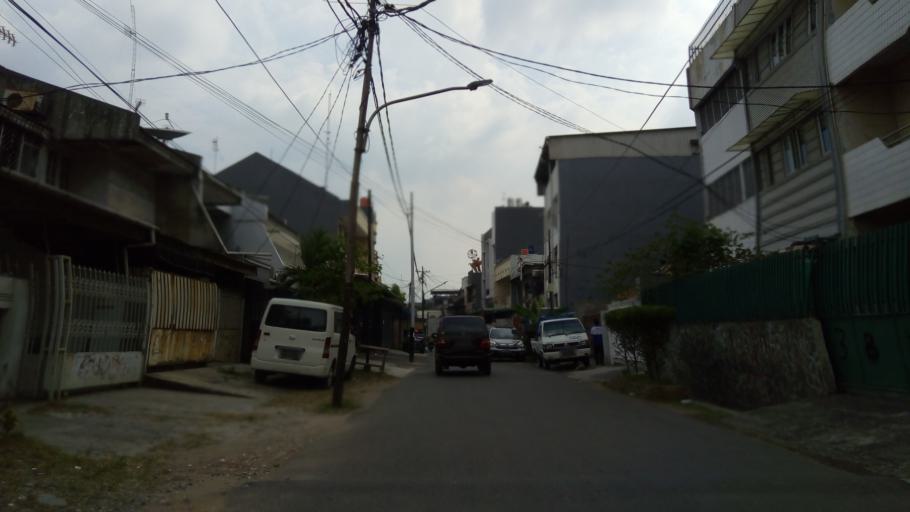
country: ID
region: Jakarta Raya
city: Jakarta
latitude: -6.1586
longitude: 106.8334
